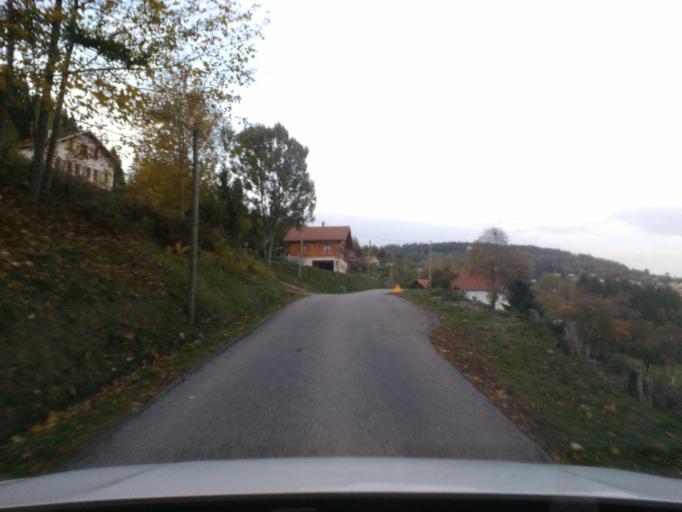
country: FR
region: Lorraine
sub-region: Departement des Vosges
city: Le Tholy
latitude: 48.0732
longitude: 6.7329
